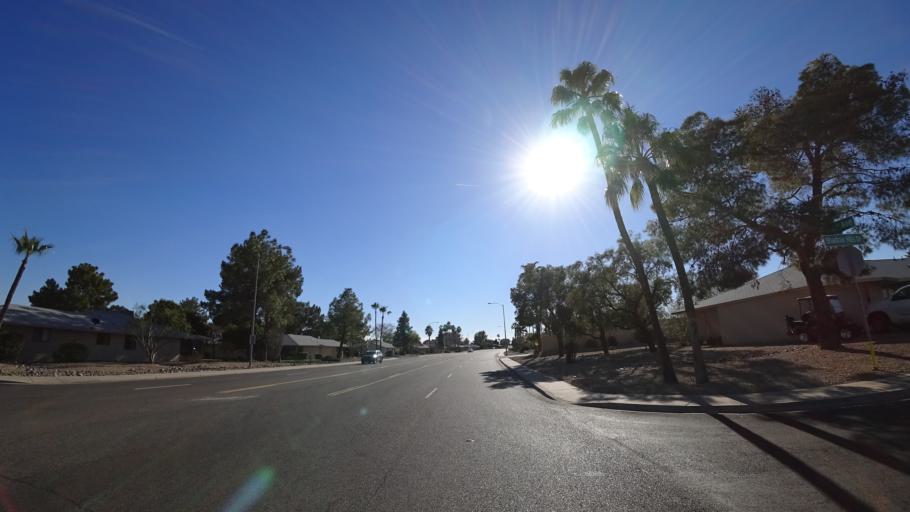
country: US
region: Arizona
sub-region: Maricopa County
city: Sun City West
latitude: 33.6540
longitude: -112.3331
